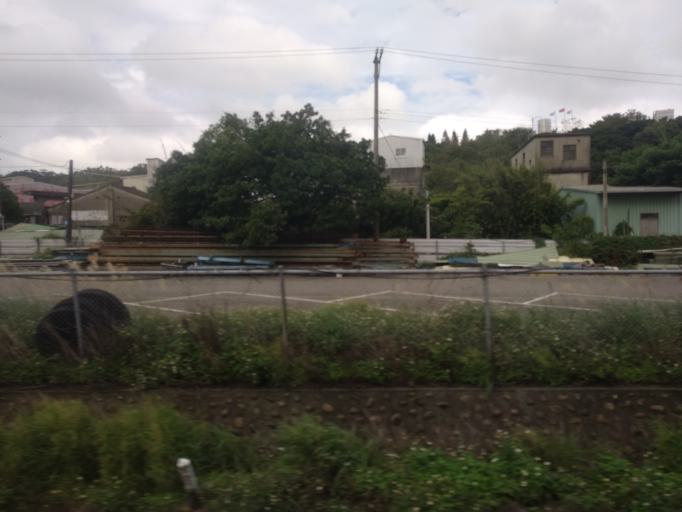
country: TW
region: Taiwan
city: Daxi
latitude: 24.9227
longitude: 121.1863
